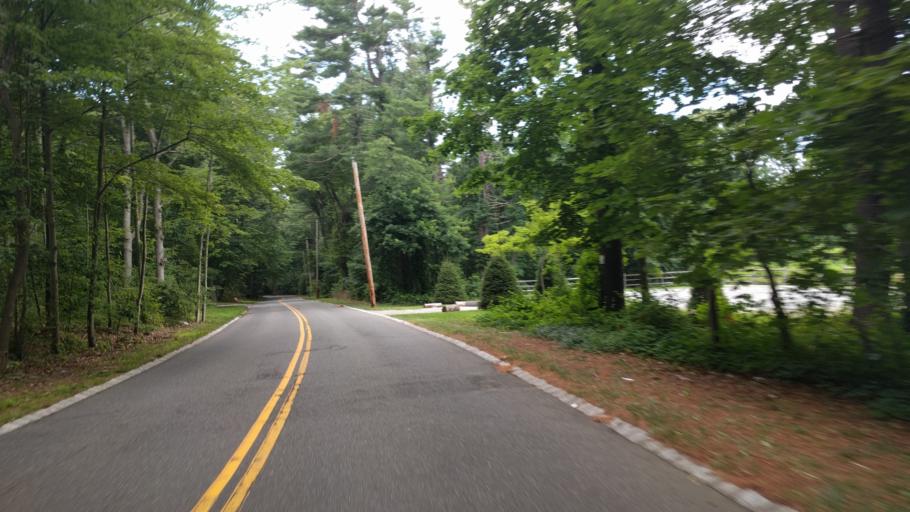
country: US
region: New York
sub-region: Nassau County
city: Oyster Bay Cove
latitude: 40.8508
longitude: -73.4965
